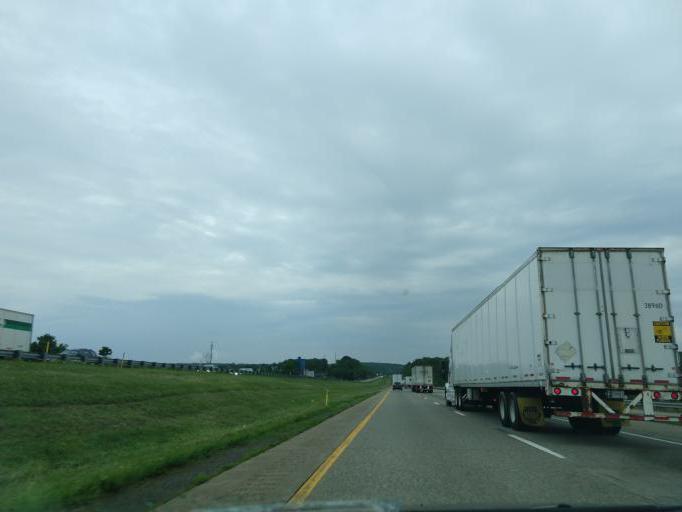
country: US
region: Pennsylvania
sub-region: Luzerne County
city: Conyngham
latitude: 40.9781
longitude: -76.0351
